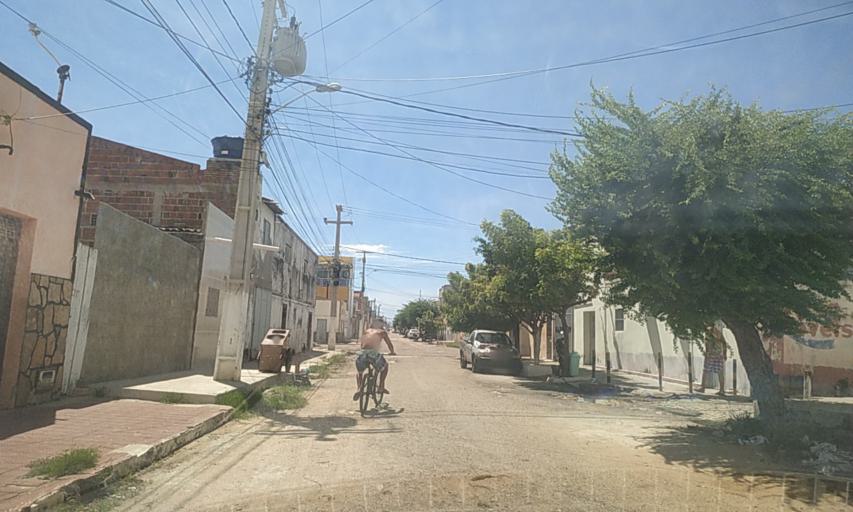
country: BR
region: Rio Grande do Norte
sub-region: Areia Branca
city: Areia Branca
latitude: -4.9592
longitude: -37.1341
